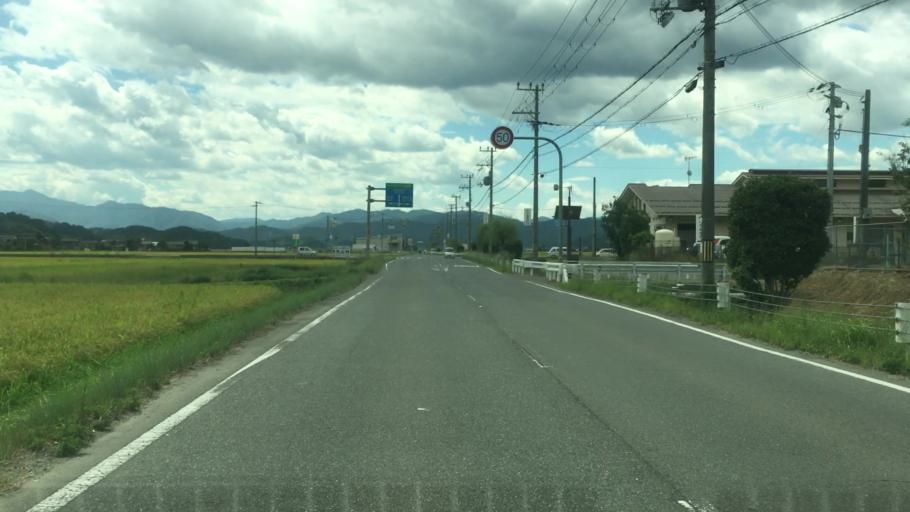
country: JP
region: Hyogo
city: Toyooka
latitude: 35.5292
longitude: 134.8398
